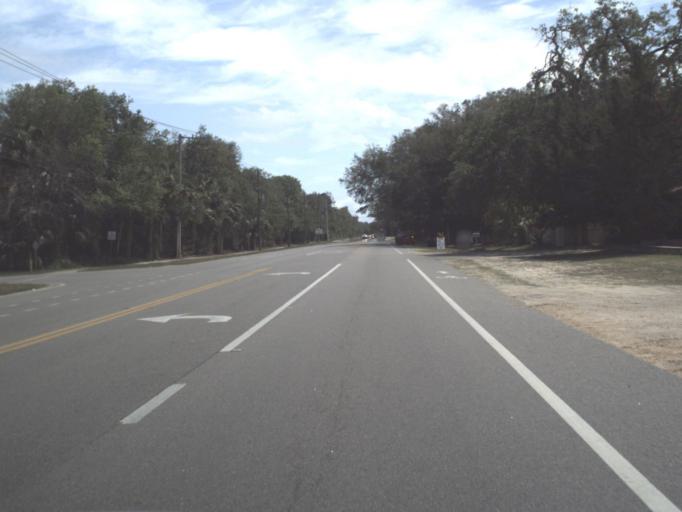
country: US
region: Florida
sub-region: Flagler County
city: Palm Coast
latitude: 29.6020
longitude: -81.1976
